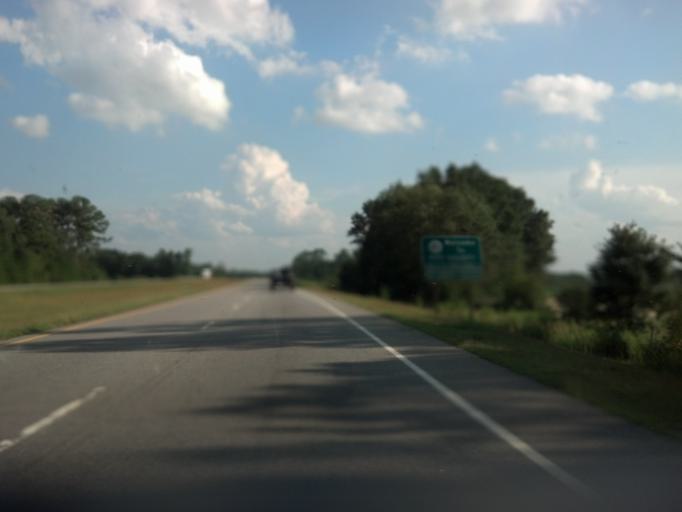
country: US
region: North Carolina
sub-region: Pitt County
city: Bethel
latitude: 35.8270
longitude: -77.3731
